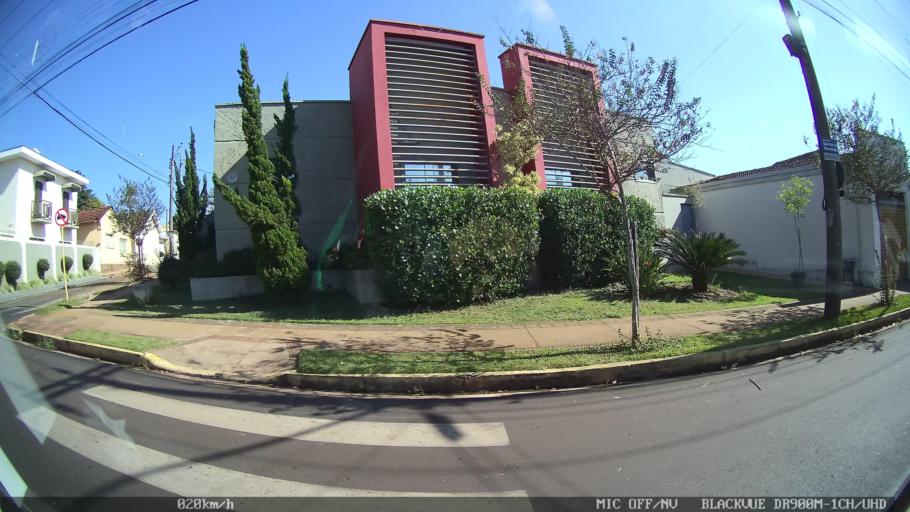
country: BR
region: Sao Paulo
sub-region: Batatais
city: Batatais
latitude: -20.8917
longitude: -47.5796
